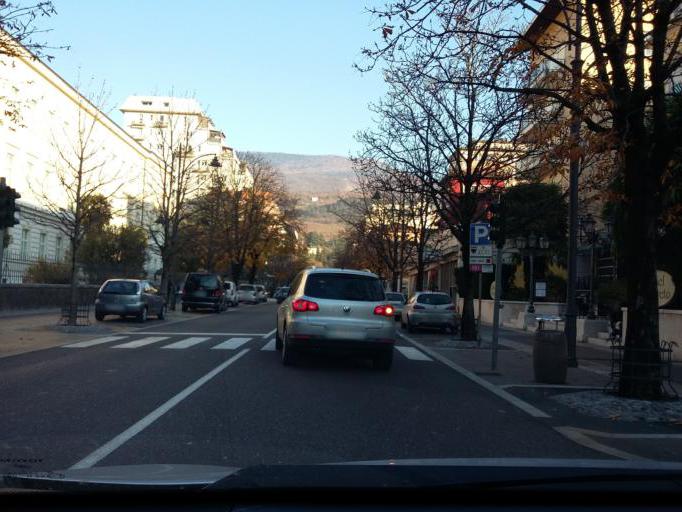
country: IT
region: Trentino-Alto Adige
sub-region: Provincia di Trento
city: Rovereto
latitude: 45.8910
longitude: 11.0374
